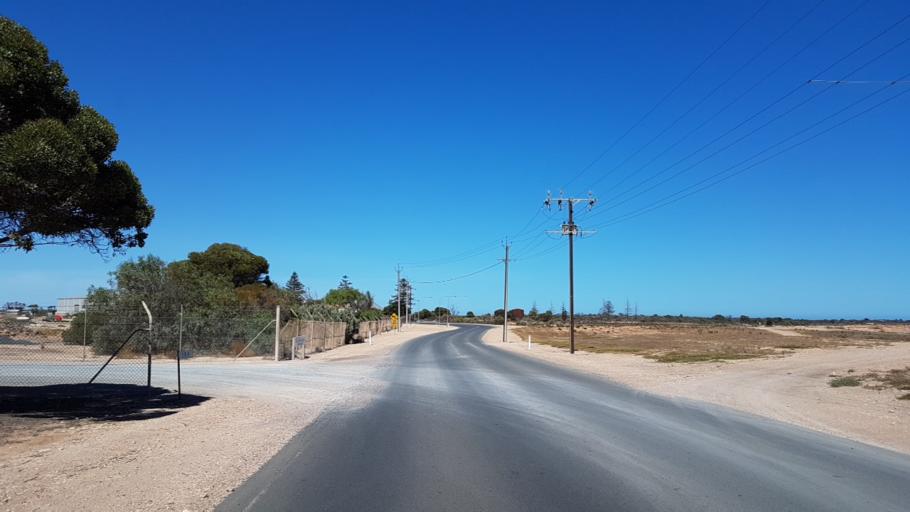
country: AU
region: South Australia
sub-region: Copper Coast
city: Wallaroo
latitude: -33.9348
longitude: 137.6095
